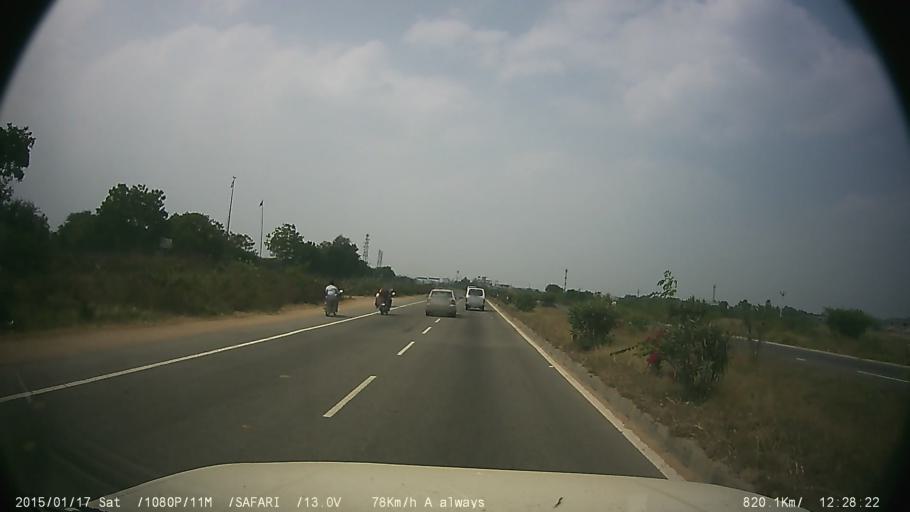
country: IN
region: Tamil Nadu
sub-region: Kancheepuram
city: Kanchipuram
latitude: 12.8727
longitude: 79.7035
